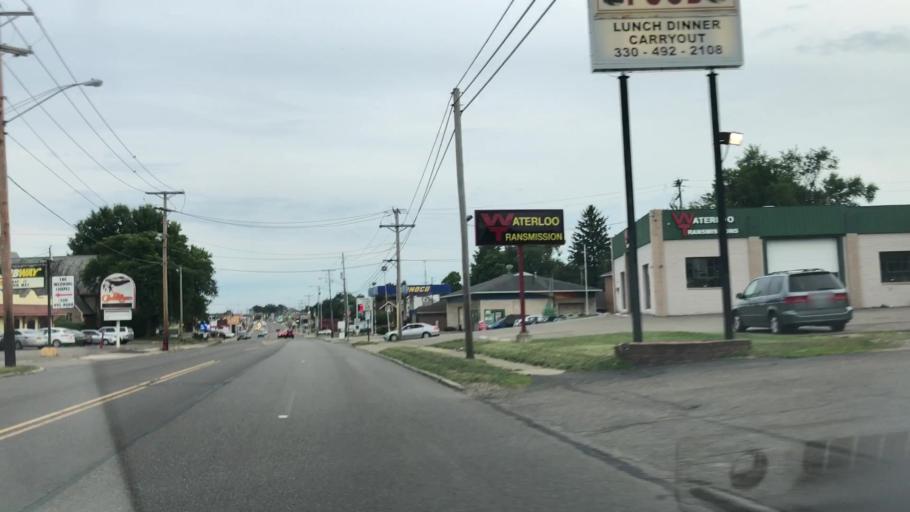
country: US
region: Ohio
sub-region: Stark County
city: North Canton
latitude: 40.8386
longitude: -81.3902
